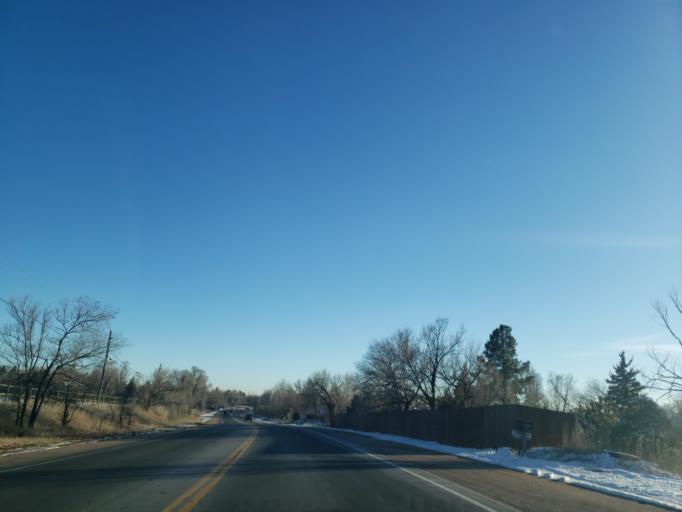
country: US
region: Colorado
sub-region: Larimer County
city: Fort Collins
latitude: 40.6341
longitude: -105.0721
